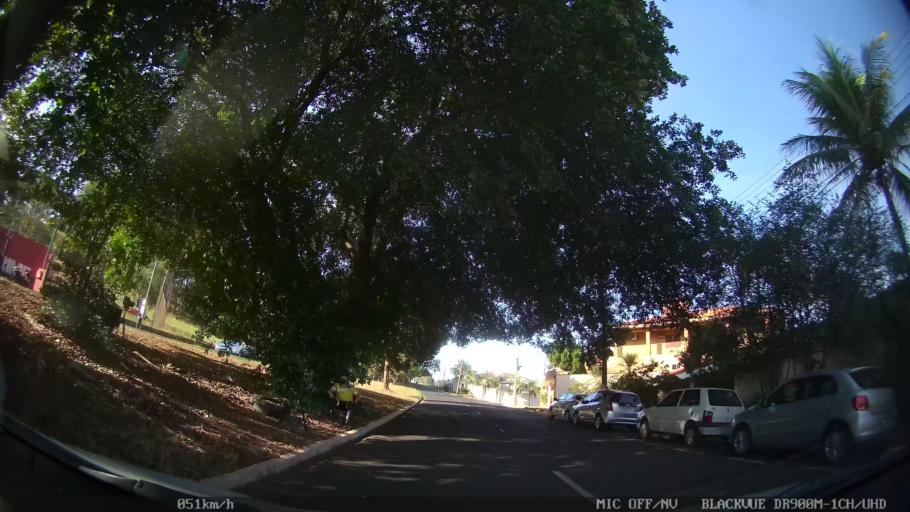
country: BR
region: Sao Paulo
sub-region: Ribeirao Preto
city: Ribeirao Preto
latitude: -21.2064
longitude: -47.7861
